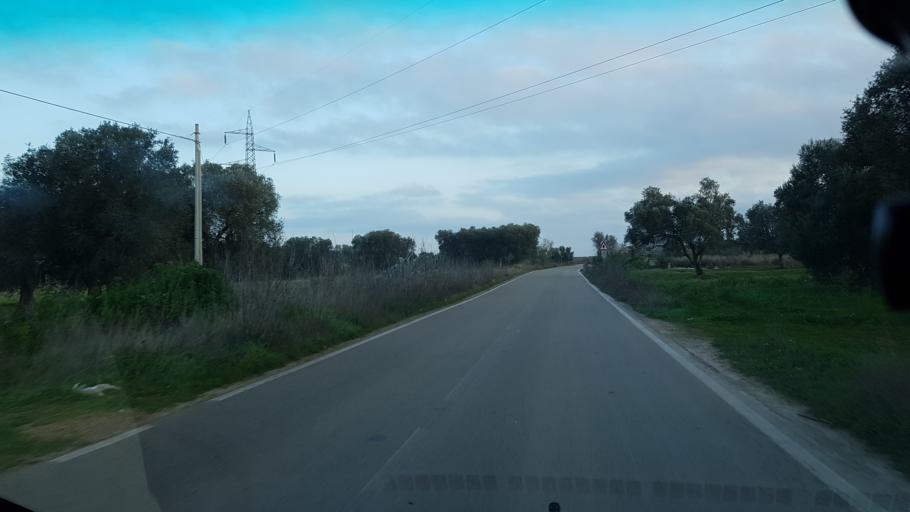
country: IT
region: Apulia
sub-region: Provincia di Brindisi
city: San Vito dei Normanni
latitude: 40.6387
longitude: 17.7799
